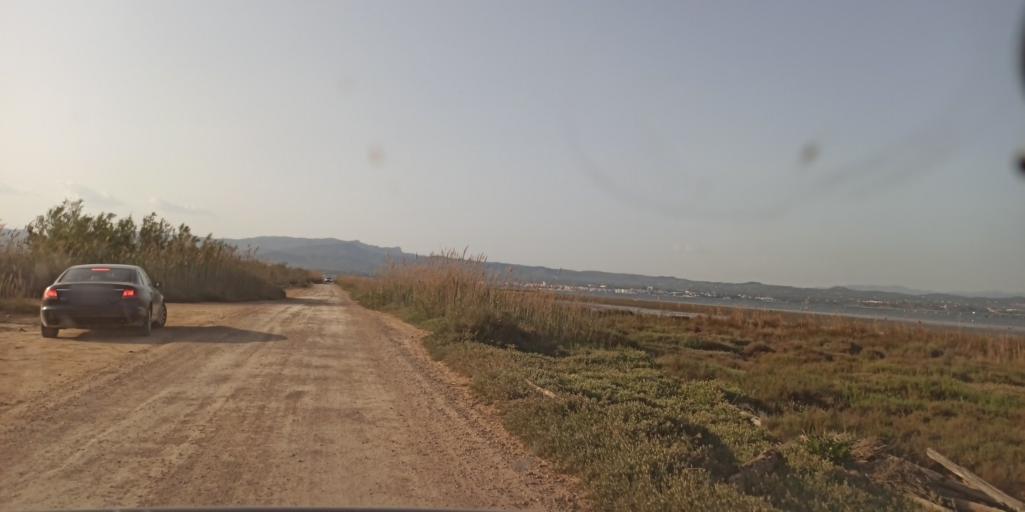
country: ES
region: Catalonia
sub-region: Provincia de Tarragona
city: L'Ampolla
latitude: 40.7752
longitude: 0.7244
